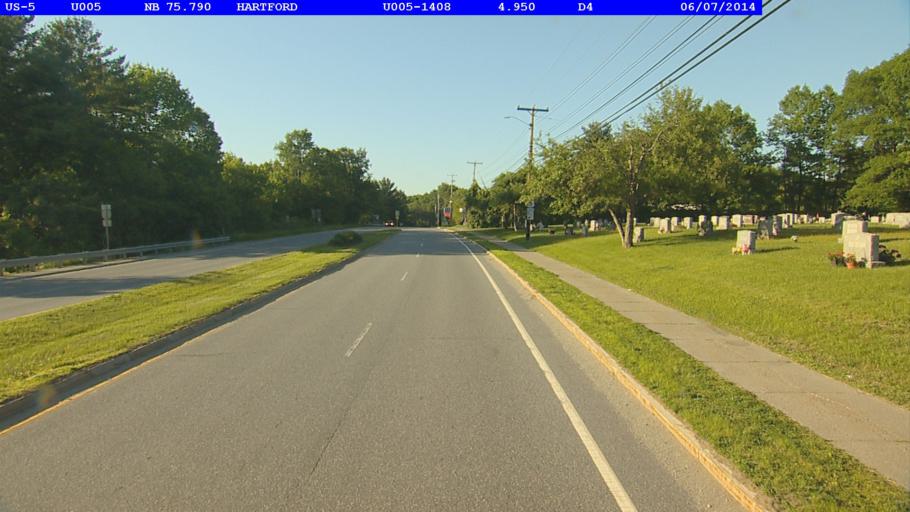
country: US
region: Vermont
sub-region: Windsor County
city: Wilder
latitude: 43.6636
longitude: -72.3130
